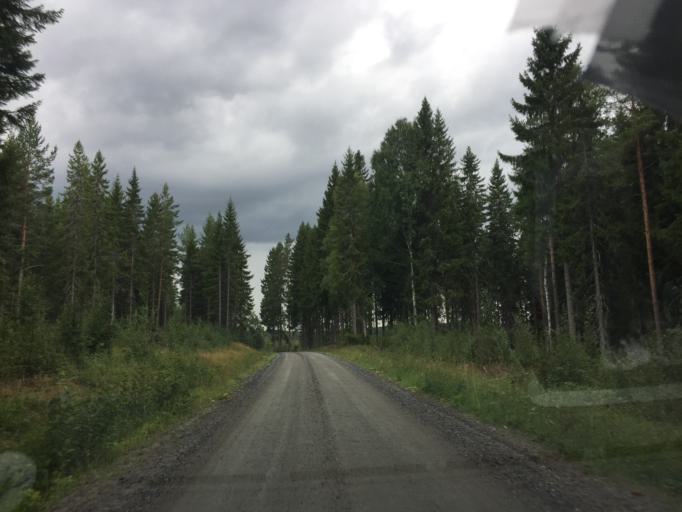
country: SE
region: Vaermland
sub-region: Filipstads Kommun
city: Lesjofors
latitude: 59.9759
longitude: 14.0933
